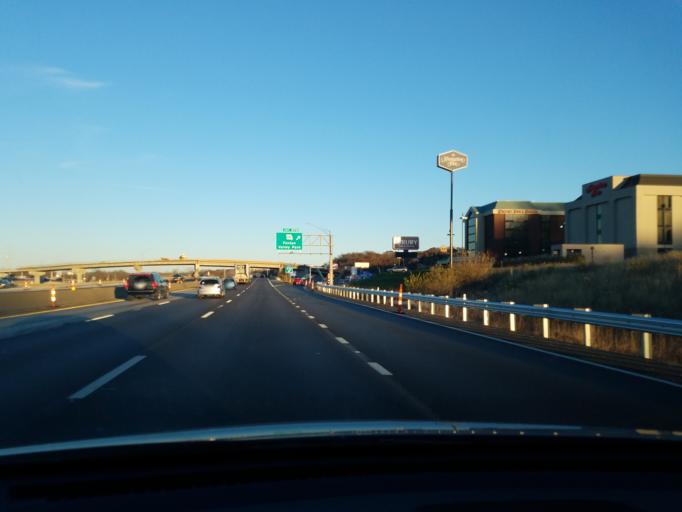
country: US
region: Missouri
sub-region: Saint Louis County
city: Valley Park
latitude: 38.5384
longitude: -90.4995
